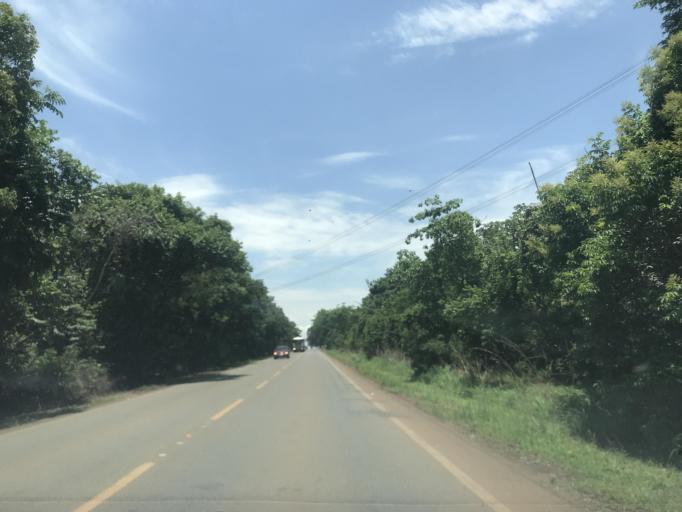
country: BR
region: Goias
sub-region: Vianopolis
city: Vianopolis
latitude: -16.6274
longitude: -48.3547
